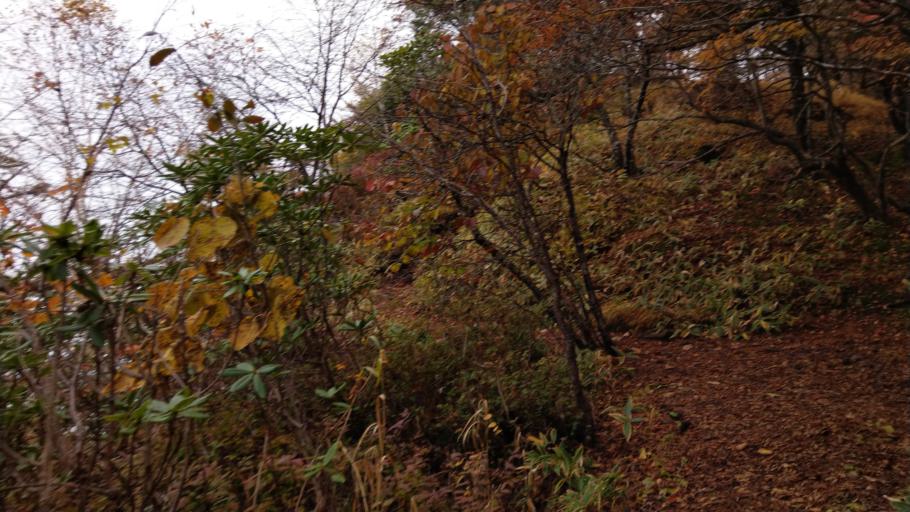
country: JP
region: Nagano
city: Komoro
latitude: 36.4027
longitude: 138.4580
